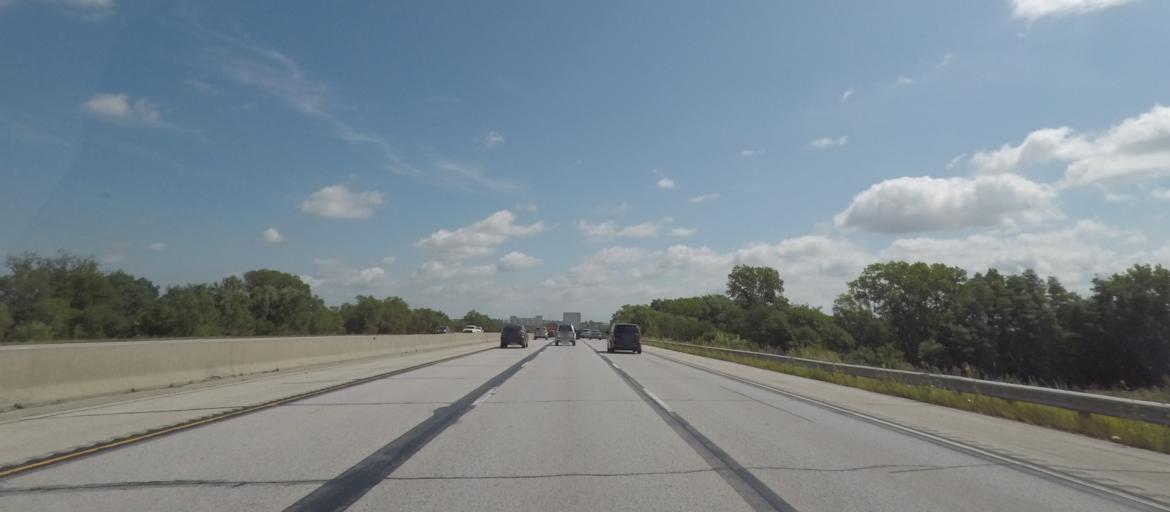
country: US
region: Iowa
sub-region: Polk County
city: Des Moines
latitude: 41.6538
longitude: -93.5633
